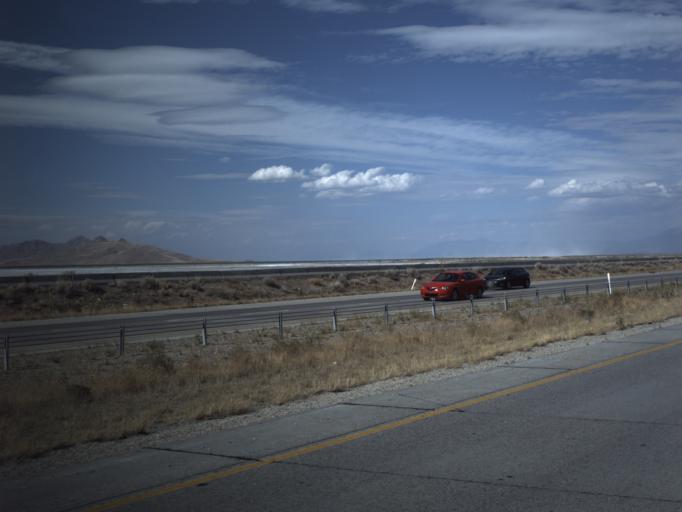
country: US
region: Utah
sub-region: Salt Lake County
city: Magna
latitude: 40.7583
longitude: -112.1672
